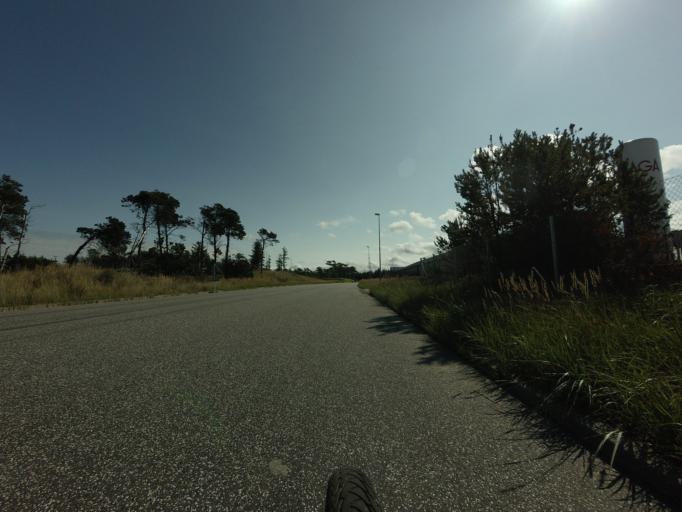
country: DK
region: North Denmark
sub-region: Hjorring Kommune
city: Hirtshals
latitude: 57.5864
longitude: 9.9844
